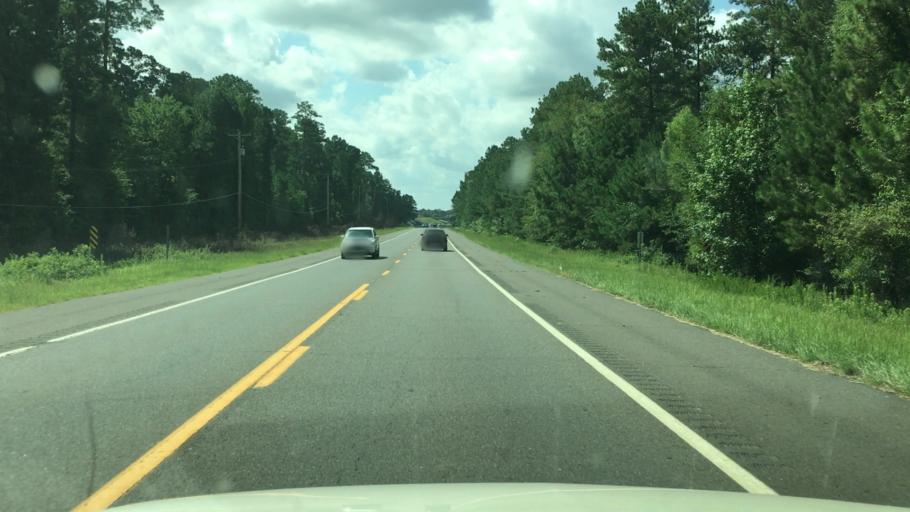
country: US
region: Arkansas
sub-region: Clark County
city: Arkadelphia
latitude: 34.1942
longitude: -93.0746
